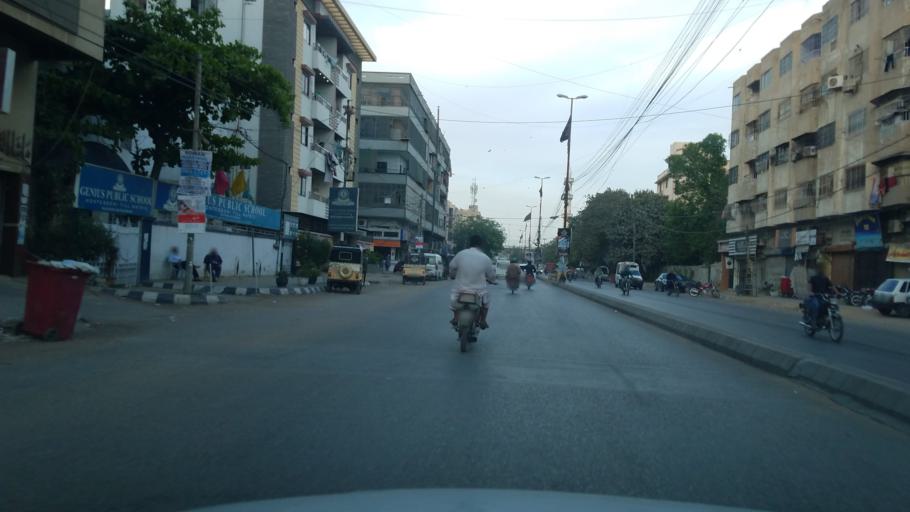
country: PK
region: Sindh
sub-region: Karachi District
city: Karachi
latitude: 24.8782
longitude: 67.0363
